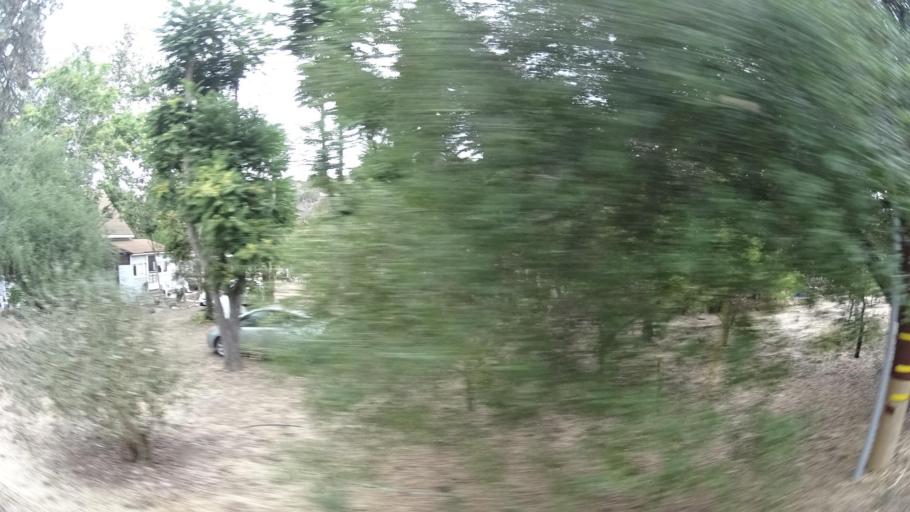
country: US
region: California
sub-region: San Diego County
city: Ramona
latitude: 32.9821
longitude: -116.9231
